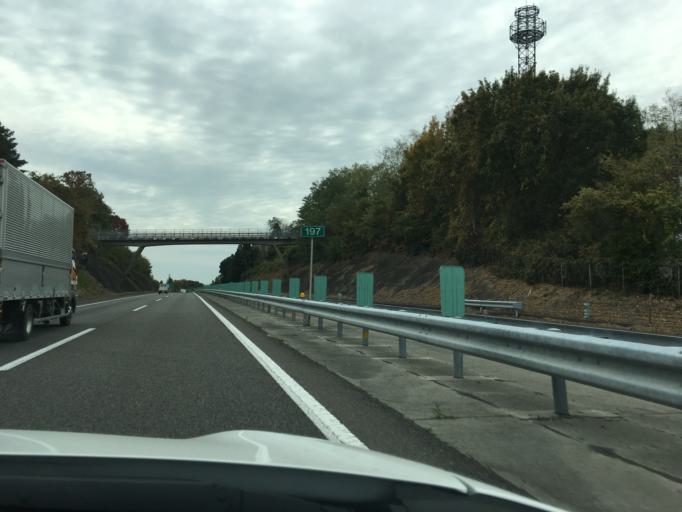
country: JP
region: Fukushima
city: Sukagawa
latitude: 37.2799
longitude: 140.3507
